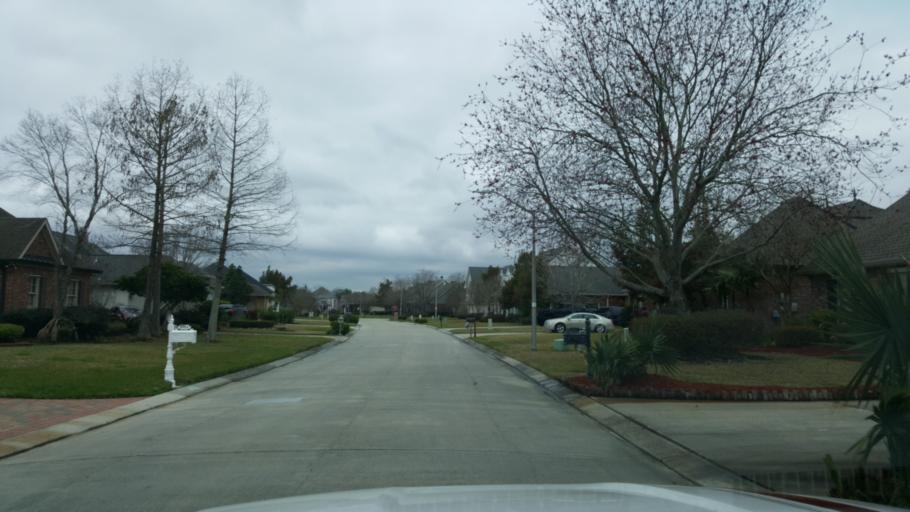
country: US
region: Louisiana
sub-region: Jefferson Parish
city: Woodmere
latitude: 29.8778
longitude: -90.0781
